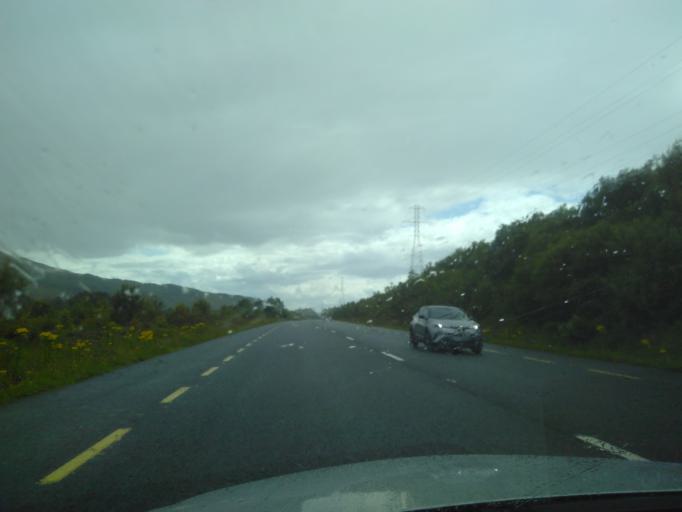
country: IE
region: Ulster
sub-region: County Donegal
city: Donegal
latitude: 54.7131
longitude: -7.9653
